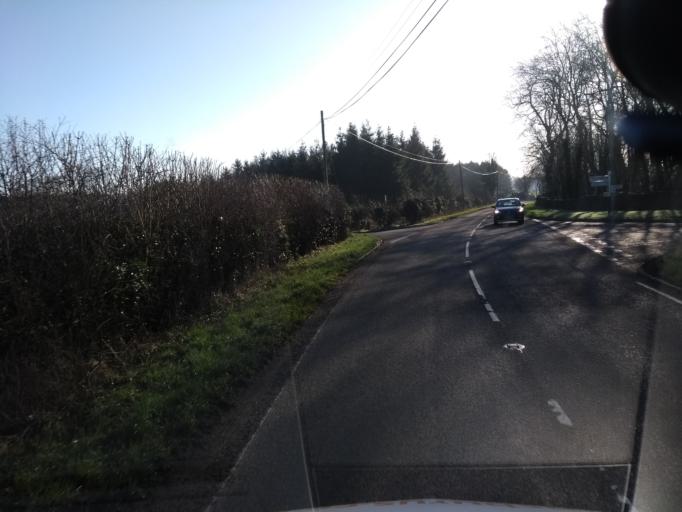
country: GB
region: England
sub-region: Somerset
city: Redlynch
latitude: 51.0994
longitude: -2.4268
